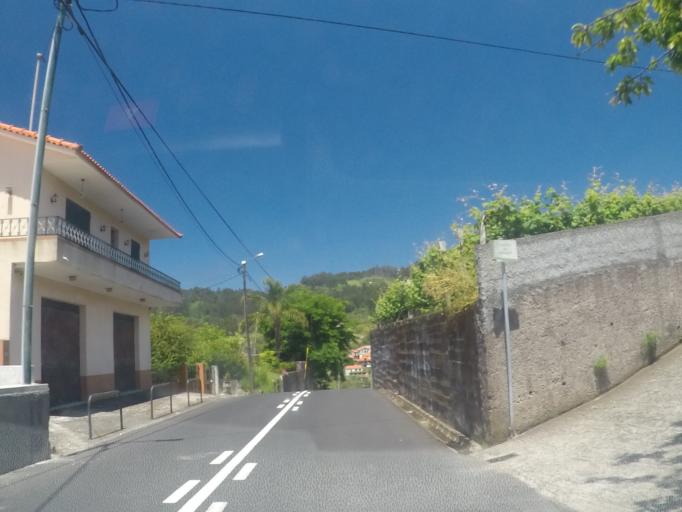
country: PT
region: Madeira
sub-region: Camara de Lobos
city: Curral das Freiras
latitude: 32.6855
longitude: -16.9913
